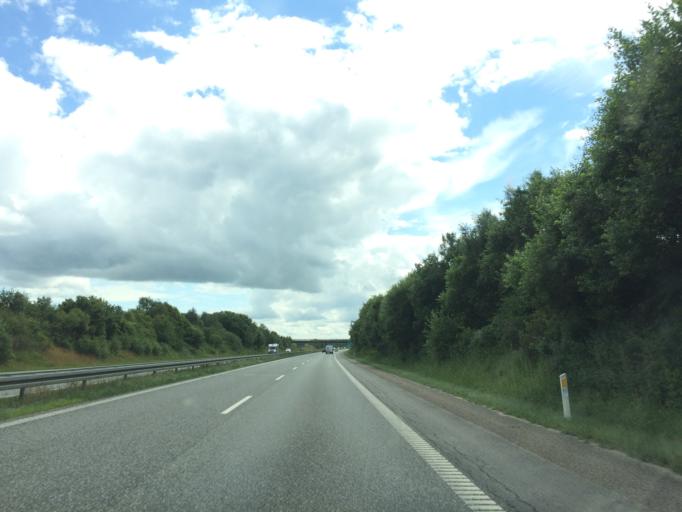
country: DK
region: North Denmark
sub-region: Mariagerfjord Kommune
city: Hobro
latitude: 56.6567
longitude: 9.7366
